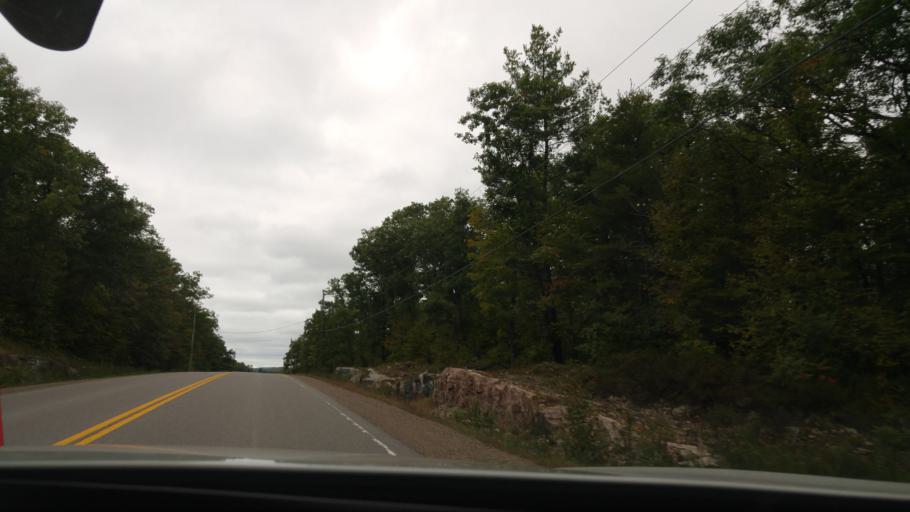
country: CA
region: Ontario
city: Petawawa
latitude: 45.8210
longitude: -77.3039
